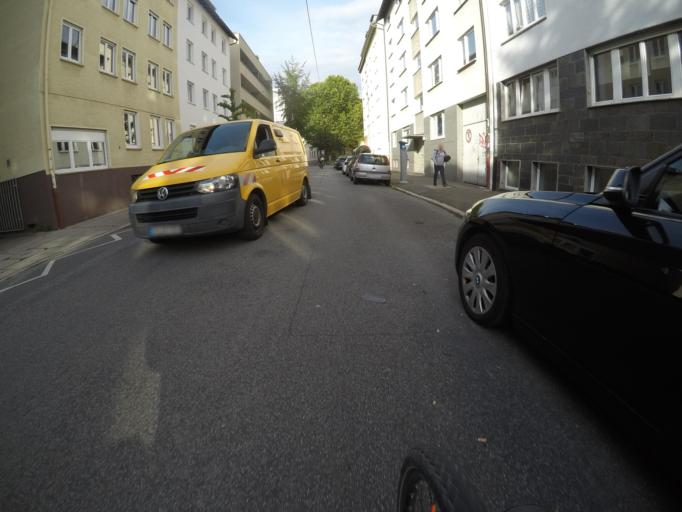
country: DE
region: Baden-Wuerttemberg
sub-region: Regierungsbezirk Stuttgart
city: Stuttgart
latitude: 48.7755
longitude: 9.1663
